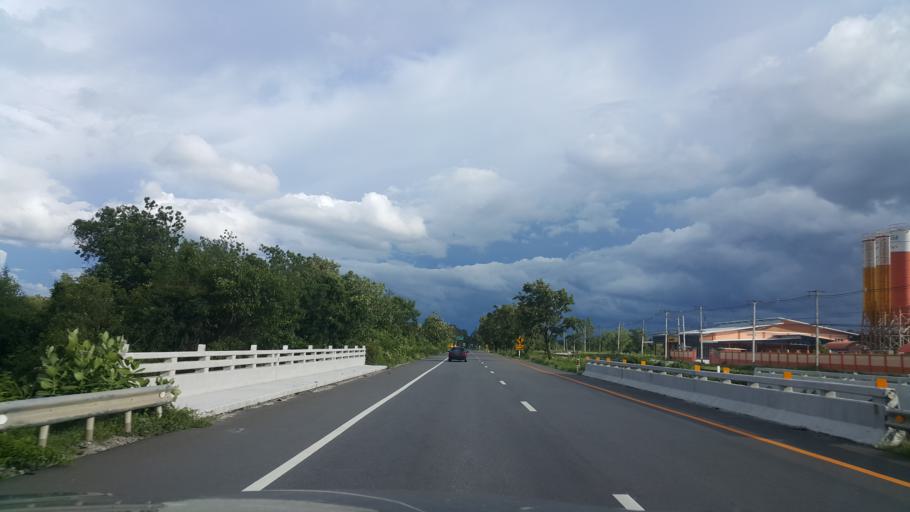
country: TH
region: Tak
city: Ban Tak
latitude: 16.9680
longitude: 99.1311
